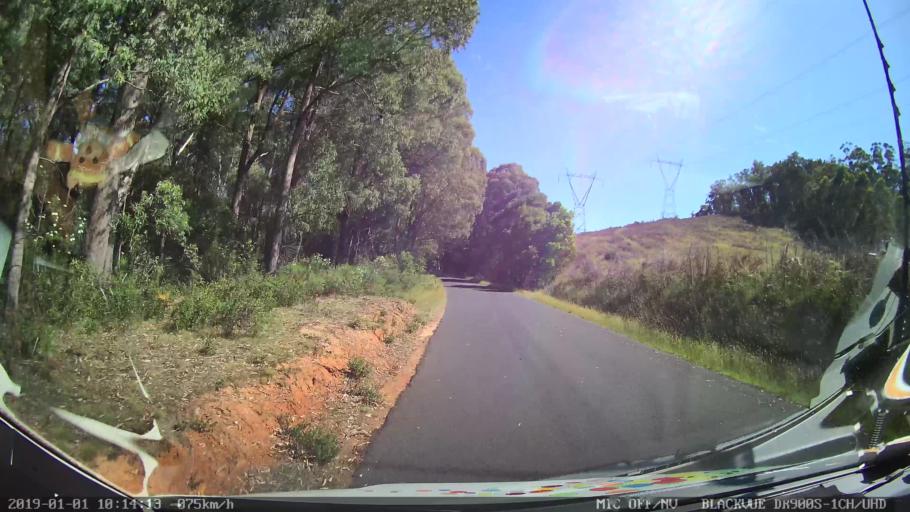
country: AU
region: New South Wales
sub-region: Snowy River
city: Jindabyne
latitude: -36.1145
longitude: 148.1610
